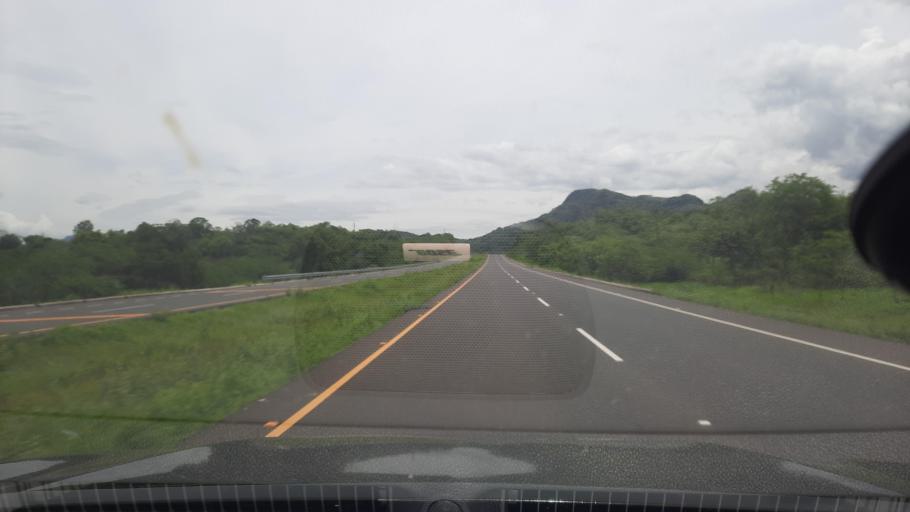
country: HN
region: Valle
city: Aramecina
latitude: 13.7781
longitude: -87.6993
